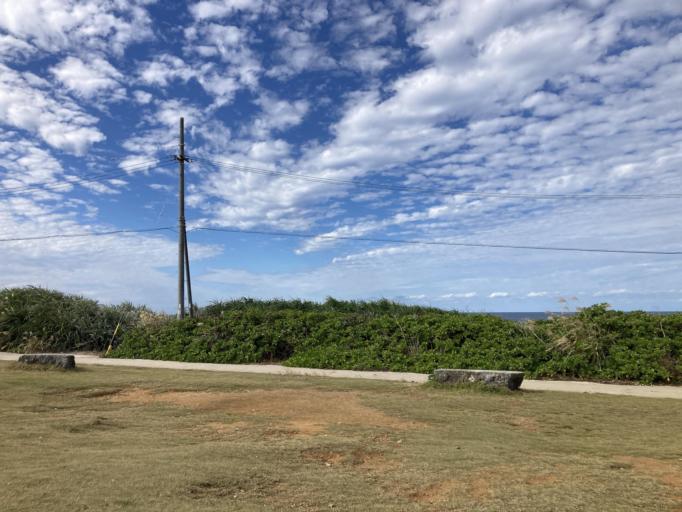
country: JP
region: Okinawa
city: Ishikawa
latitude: 26.4403
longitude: 127.7142
